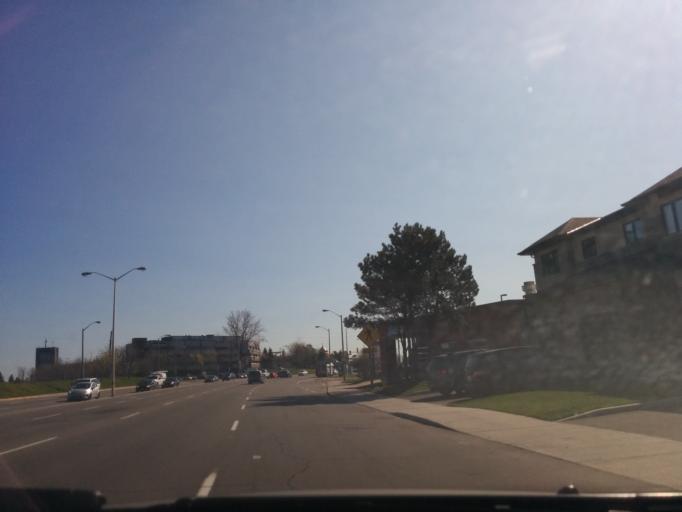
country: CA
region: Ontario
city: Ottawa
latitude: 45.3743
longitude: -75.7097
